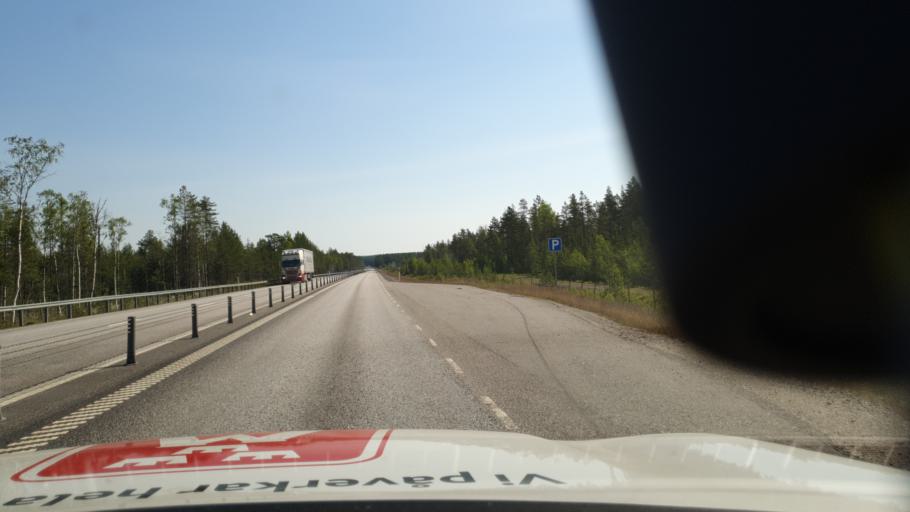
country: SE
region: Vaesterbotten
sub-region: Umea Kommun
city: Saevar
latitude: 63.9892
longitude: 20.7487
